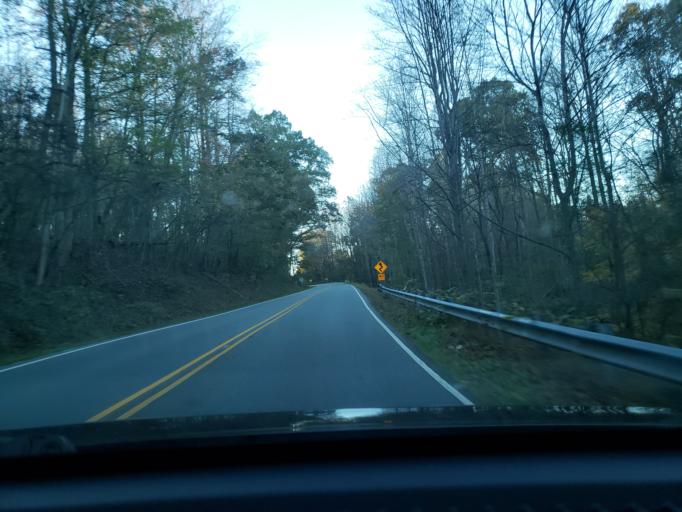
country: US
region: North Carolina
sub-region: Stokes County
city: Danbury
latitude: 36.3944
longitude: -80.1973
